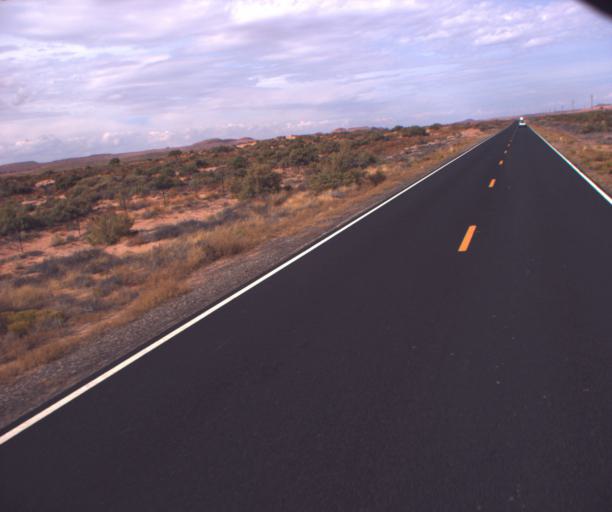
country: US
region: Arizona
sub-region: Apache County
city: Many Farms
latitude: 36.6446
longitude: -109.5900
